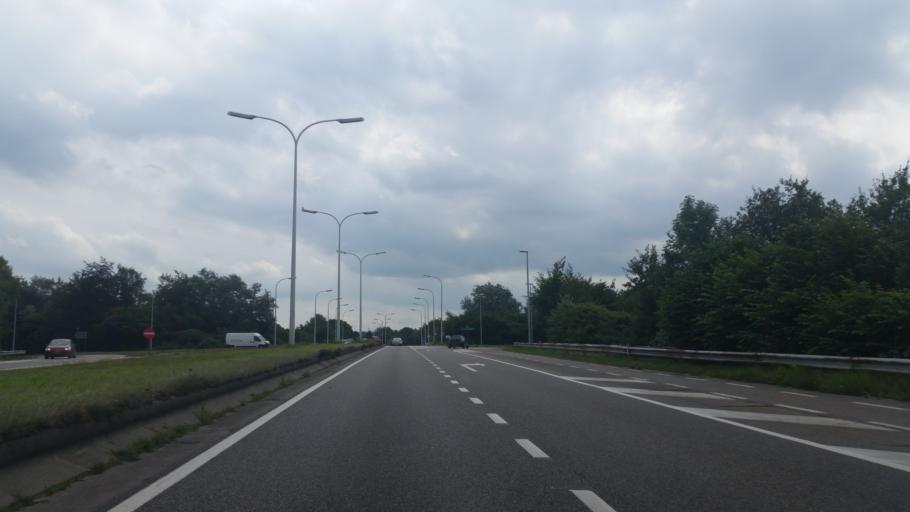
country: BE
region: Flanders
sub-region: Provincie Antwerpen
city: Turnhout
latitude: 51.3001
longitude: 4.9512
